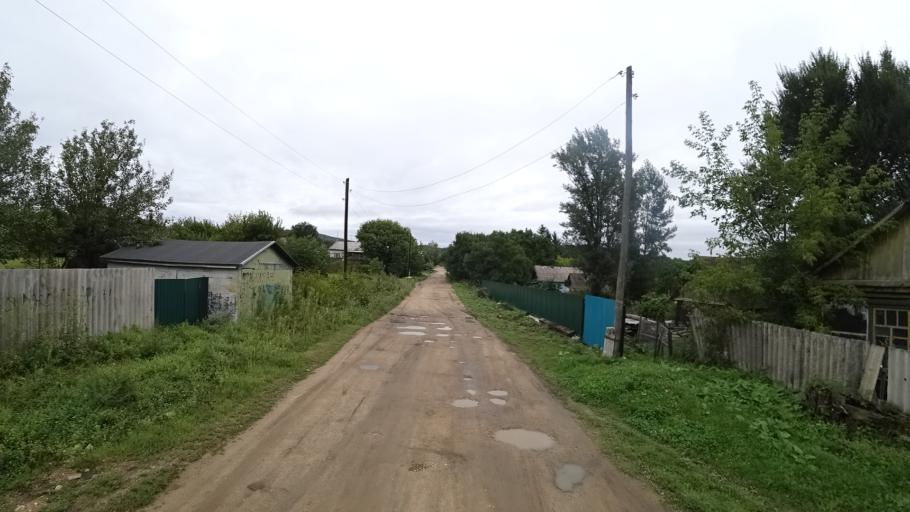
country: RU
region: Primorskiy
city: Rettikhovka
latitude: 44.1702
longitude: 132.7674
